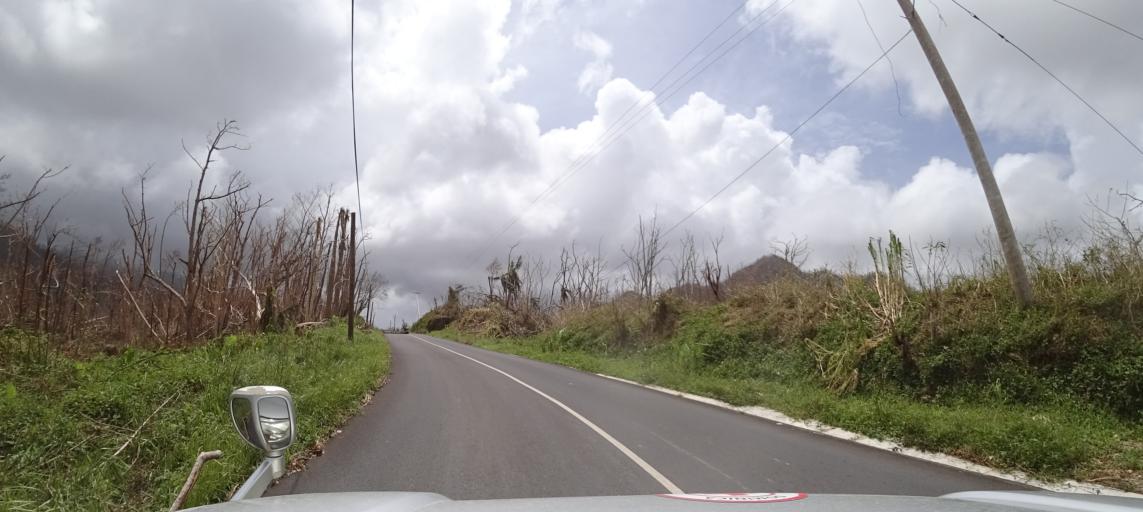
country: DM
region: Saint Paul
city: Pont Casse
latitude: 15.4200
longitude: -61.3405
